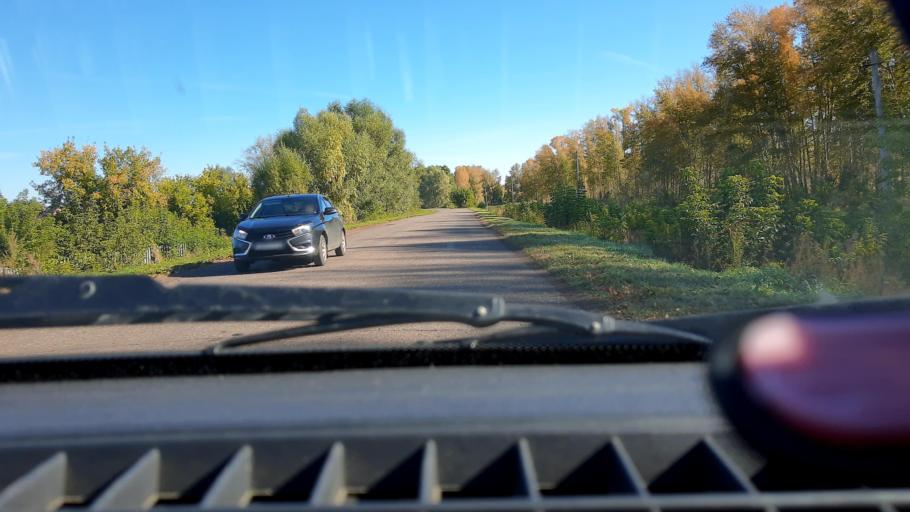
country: RU
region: Bashkortostan
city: Kushnarenkovo
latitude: 55.1031
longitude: 55.5159
